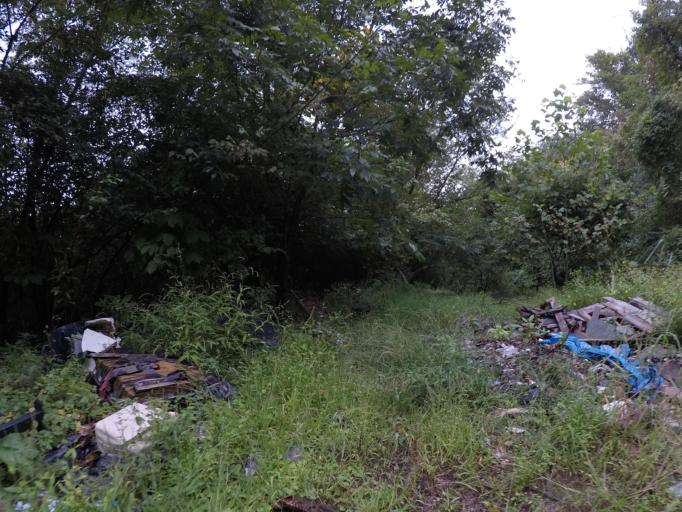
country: US
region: West Virginia
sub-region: Cabell County
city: Huntington
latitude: 38.4041
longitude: -82.4769
